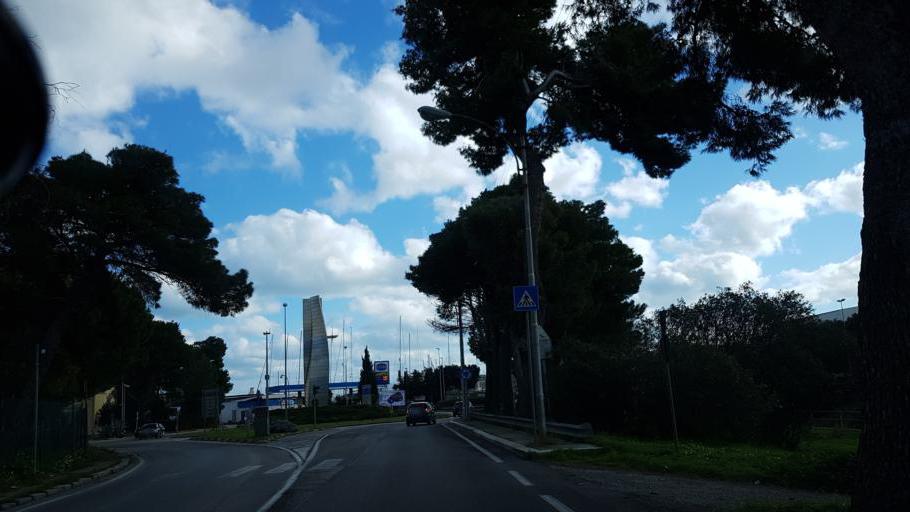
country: IT
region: Apulia
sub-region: Provincia di Brindisi
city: Brindisi
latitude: 40.6404
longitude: 17.9257
